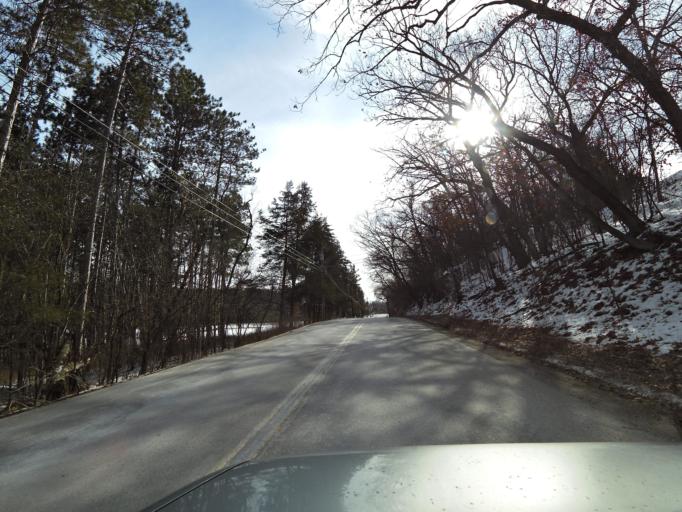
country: US
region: Minnesota
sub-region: Washington County
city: Afton
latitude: 44.9081
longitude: -92.7842
